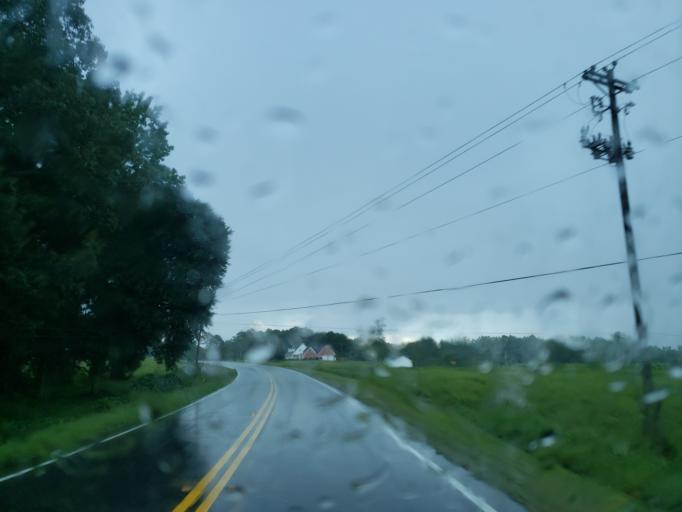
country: US
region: Georgia
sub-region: Cherokee County
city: Canton
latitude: 34.3045
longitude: -84.4579
